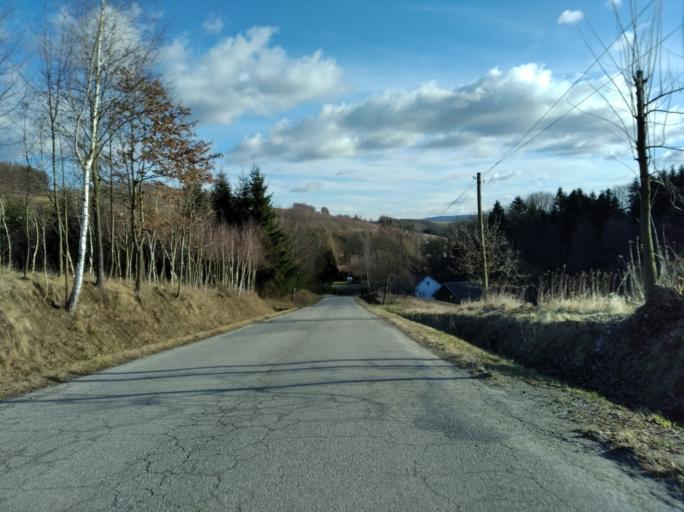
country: PL
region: Subcarpathian Voivodeship
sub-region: Powiat strzyzowski
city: Wisniowa
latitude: 49.8943
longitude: 21.7094
